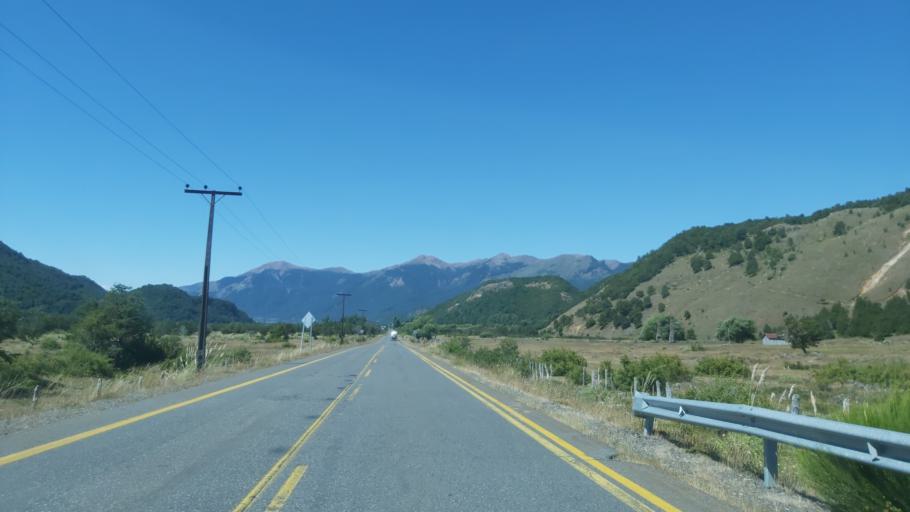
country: CL
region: Araucania
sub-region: Provincia de Cautin
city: Vilcun
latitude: -38.5673
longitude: -71.4910
